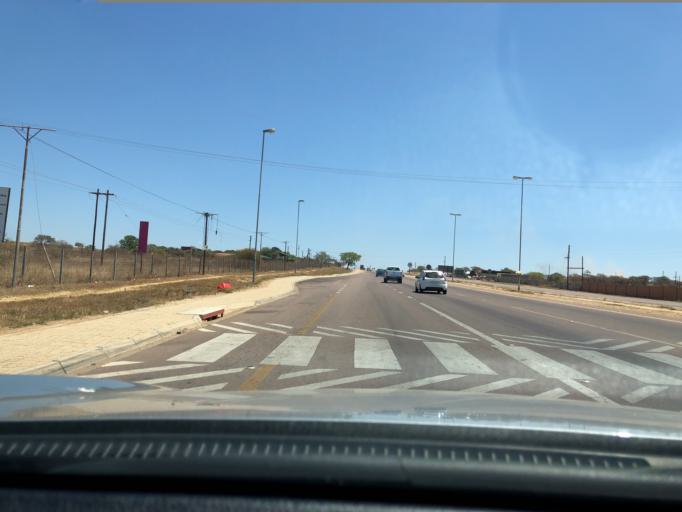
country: ZA
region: Limpopo
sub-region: Capricorn District Municipality
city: Polokwane
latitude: -23.8987
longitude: 29.5226
